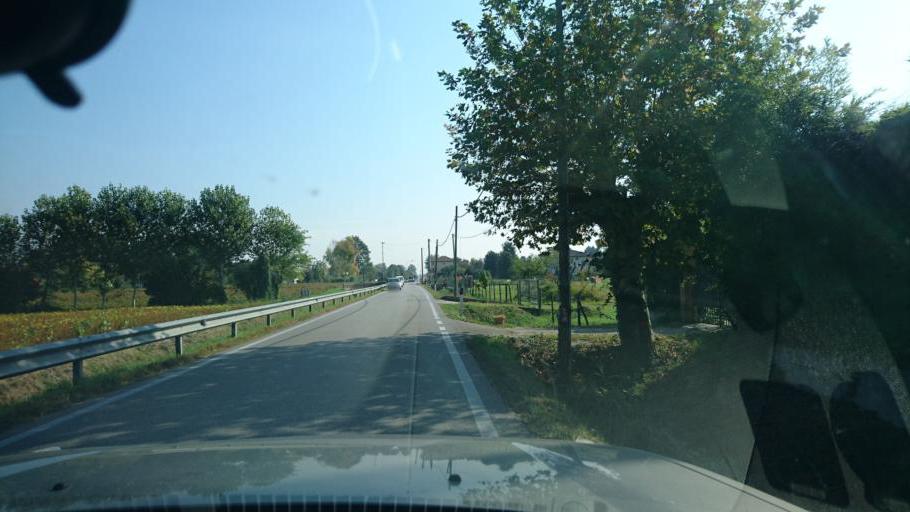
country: IT
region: Veneto
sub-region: Provincia di Padova
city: Rubano
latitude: 45.4184
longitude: 11.7842
